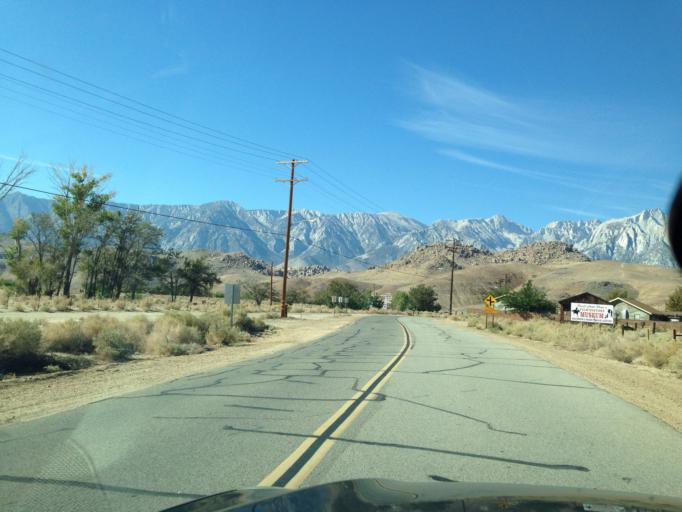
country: US
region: California
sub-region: Inyo County
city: Lone Pine
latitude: 36.6029
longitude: -118.0694
